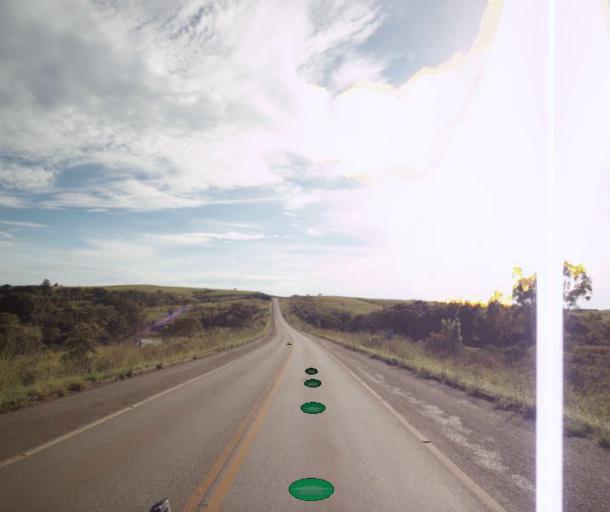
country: BR
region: Goias
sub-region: Abadiania
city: Abadiania
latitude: -15.7822
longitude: -48.4735
